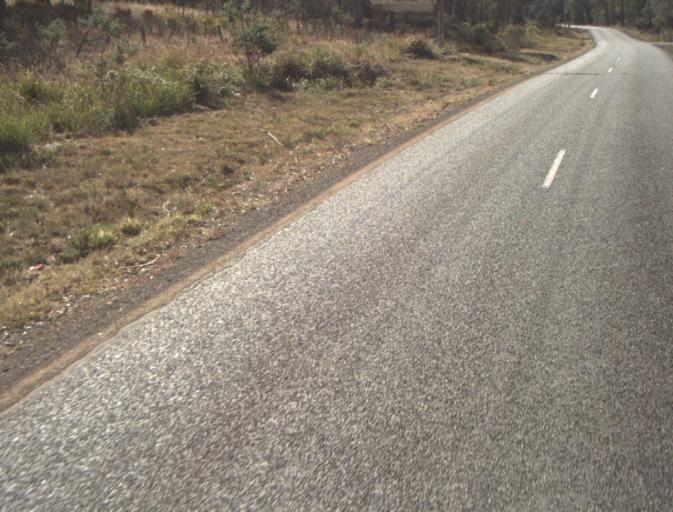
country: AU
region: Tasmania
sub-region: Launceston
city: Mayfield
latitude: -41.3317
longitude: 147.1407
